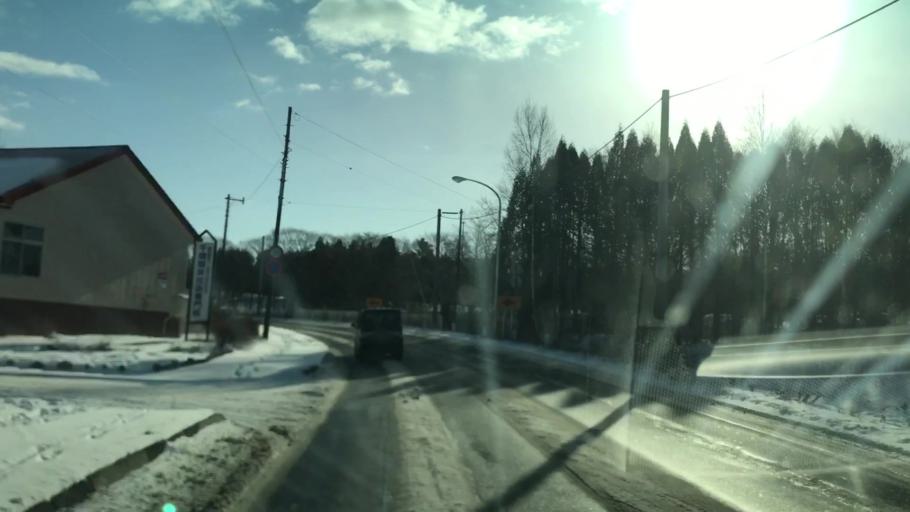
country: JP
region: Hokkaido
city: Chitose
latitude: 42.8123
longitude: 141.6425
